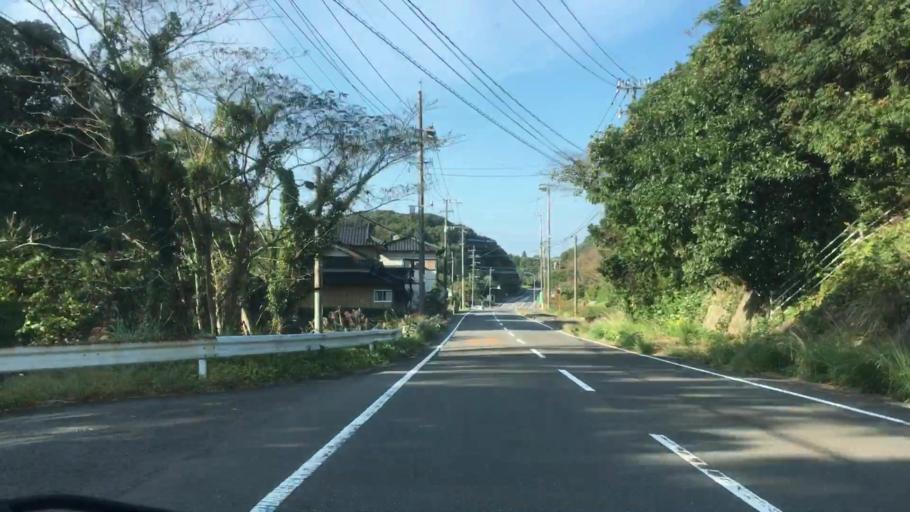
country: JP
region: Nagasaki
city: Togitsu
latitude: 32.9521
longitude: 129.6741
